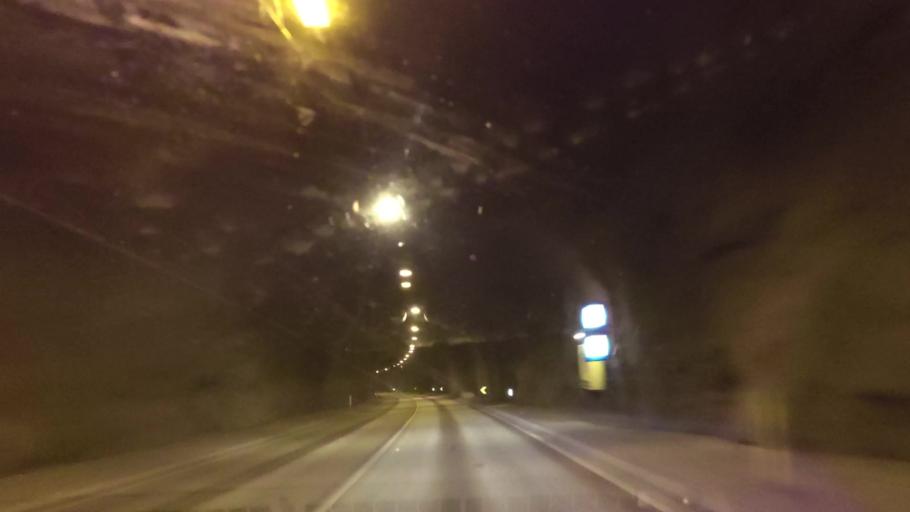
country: IS
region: Capital Region
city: Reykjavik
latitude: 64.2912
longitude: -21.8580
